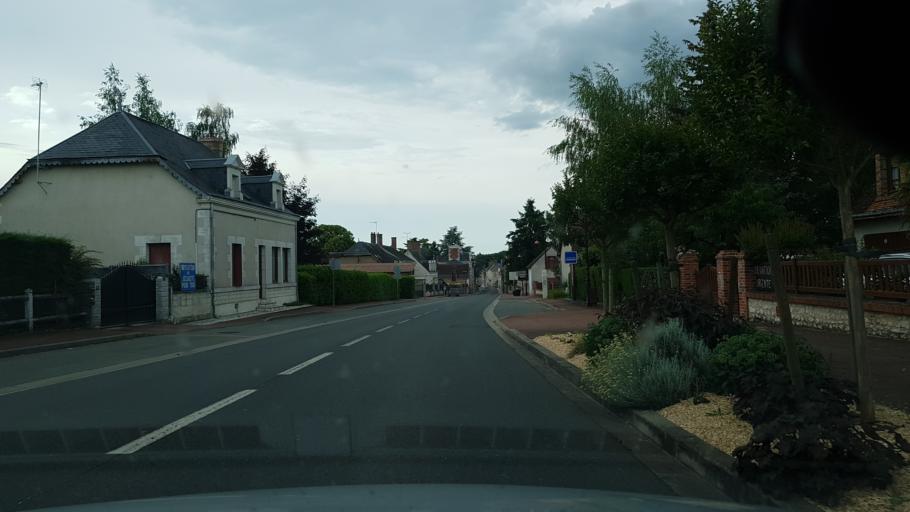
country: FR
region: Centre
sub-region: Departement du Loir-et-Cher
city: Chatillon-sur-Cher
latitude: 47.3425
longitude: 1.4799
